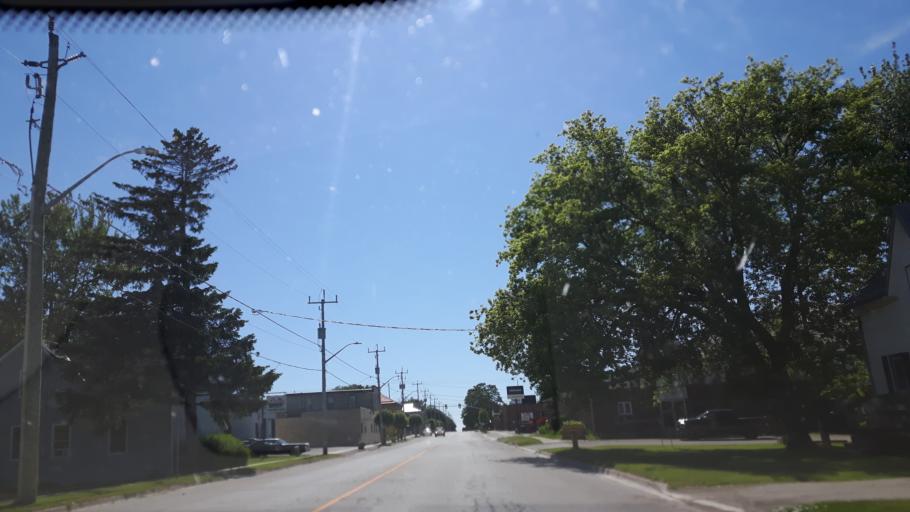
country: CA
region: Ontario
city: Bluewater
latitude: 43.4215
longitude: -81.6224
